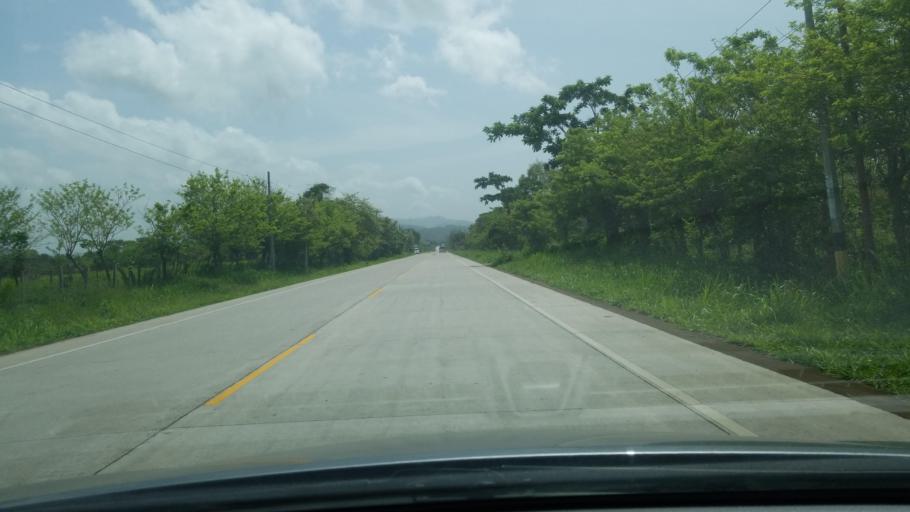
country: HN
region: Copan
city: Florida
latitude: 15.0517
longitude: -88.8009
